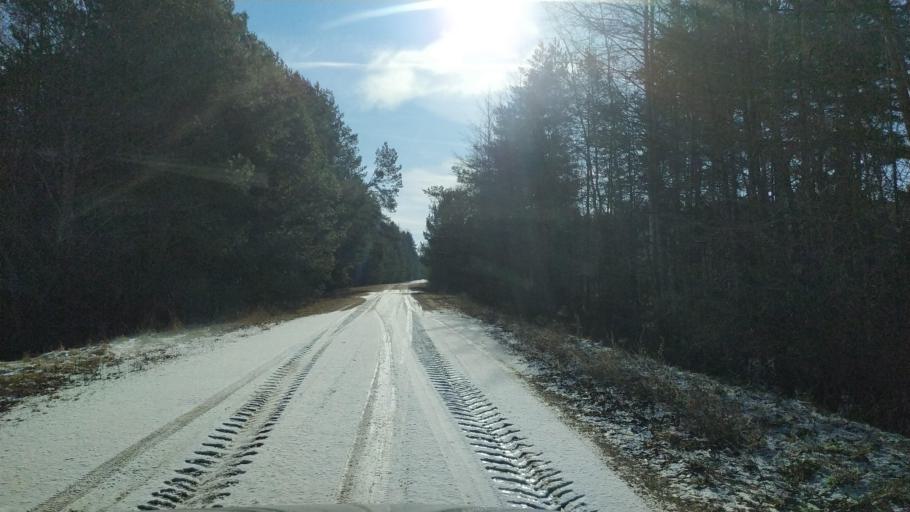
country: BY
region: Brest
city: Zhabinka
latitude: 52.4532
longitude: 24.1400
